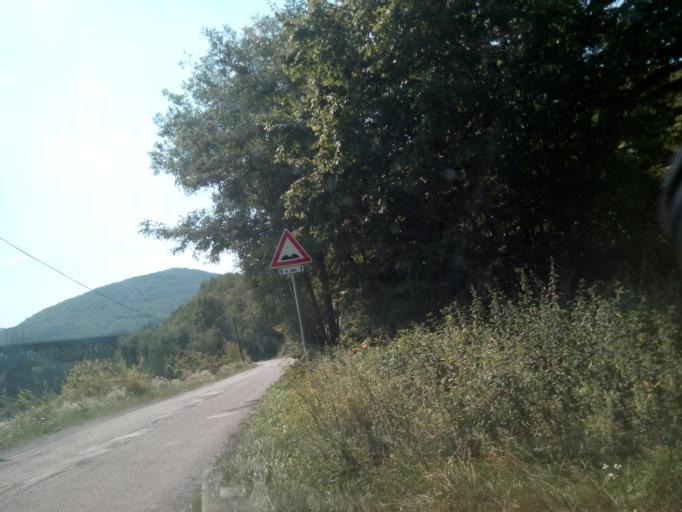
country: SK
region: Presovsky
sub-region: Okres Presov
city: Presov
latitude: 48.8784
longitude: 21.1110
